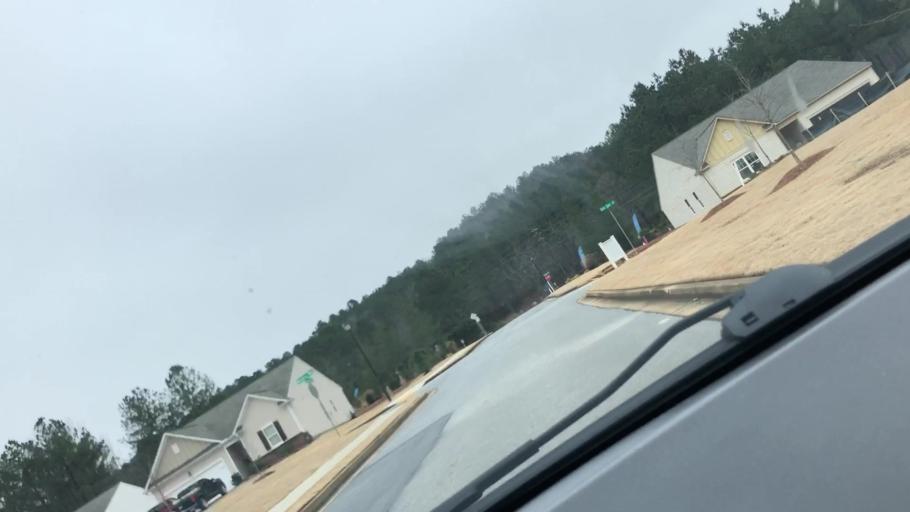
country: US
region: Georgia
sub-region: Bartow County
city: Cartersville
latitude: 34.1180
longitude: -84.8270
